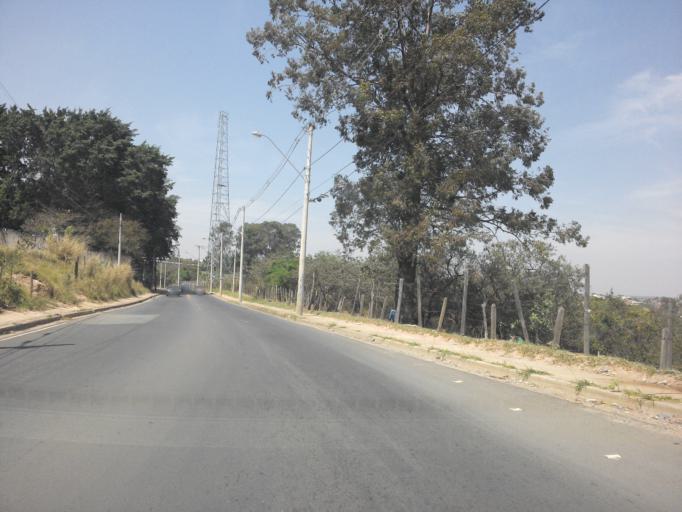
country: BR
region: Sao Paulo
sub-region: Hortolandia
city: Hortolandia
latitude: -22.9361
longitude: -47.1874
